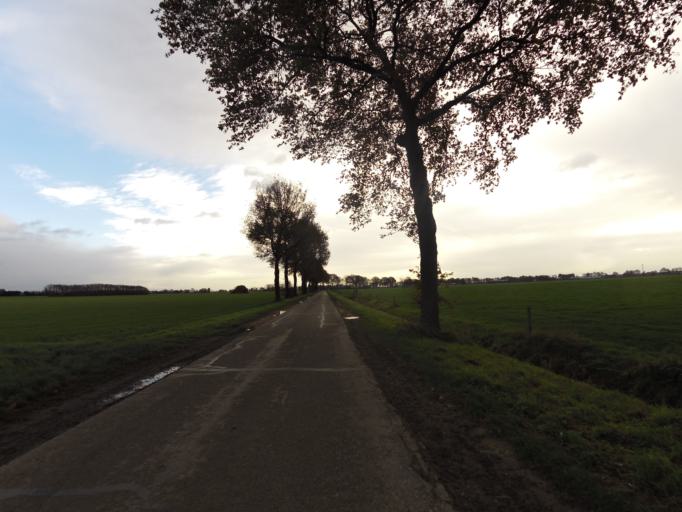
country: NL
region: Gelderland
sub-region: Gemeente Montferland
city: s-Heerenberg
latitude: 51.8933
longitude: 6.2796
